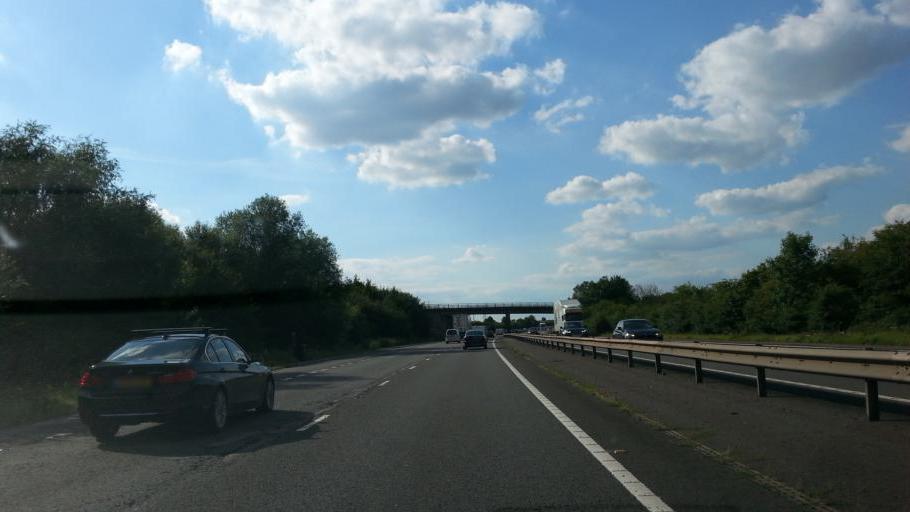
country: GB
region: England
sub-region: Lincolnshire
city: Long Bennington
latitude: 52.9803
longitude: -0.7477
